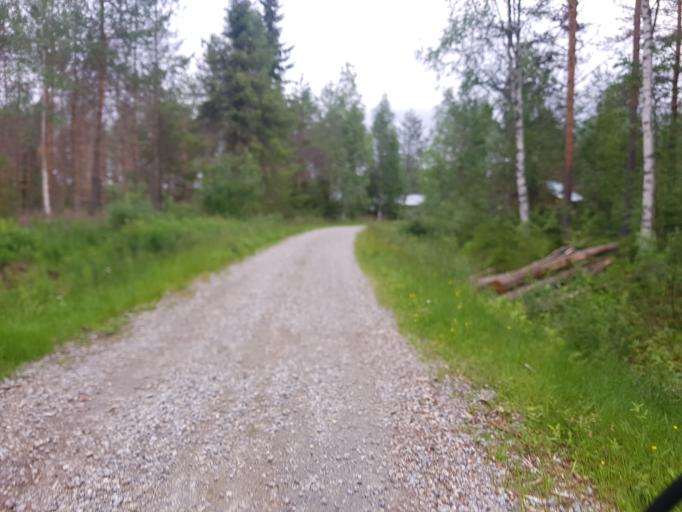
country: FI
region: Kainuu
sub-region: Kehys-Kainuu
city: Kuhmo
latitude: 64.4517
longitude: 29.7249
